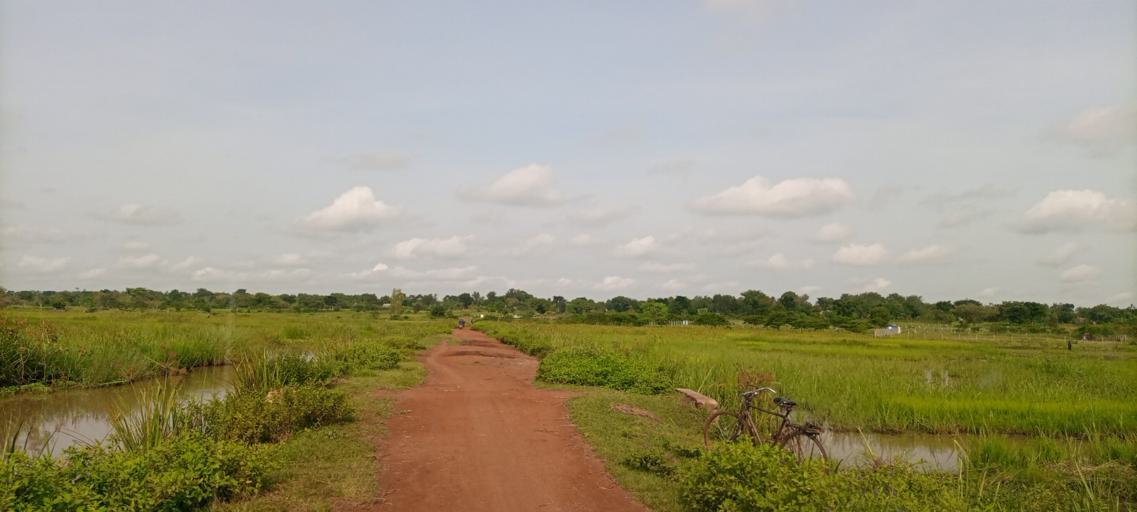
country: UG
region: Eastern Region
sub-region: Kibuku District
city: Kibuku
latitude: 1.0983
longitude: 33.7718
